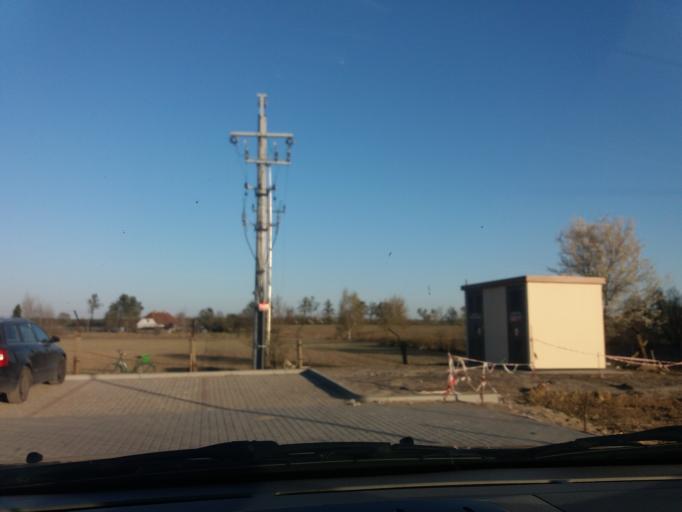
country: PL
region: Warmian-Masurian Voivodeship
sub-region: Powiat szczycienski
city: Szczytno
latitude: 53.5526
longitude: 20.9843
